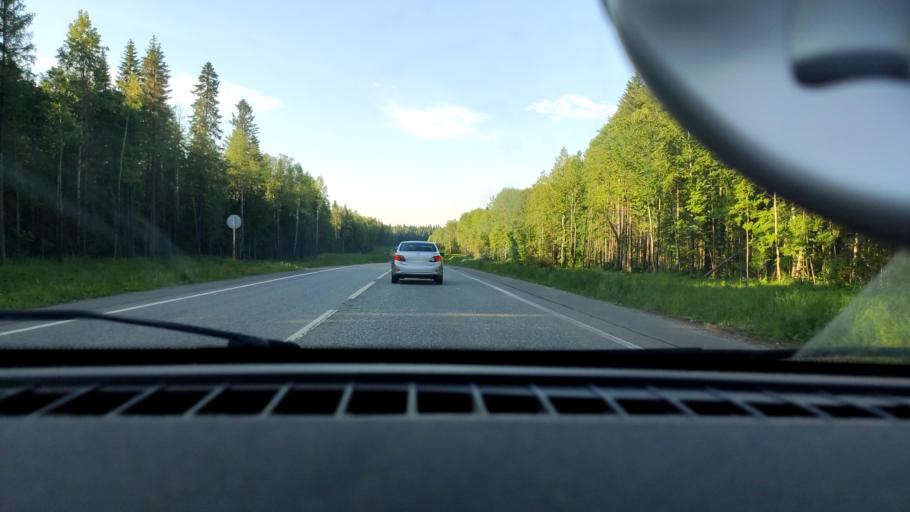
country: RU
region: Perm
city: Novyye Lyady
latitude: 58.0410
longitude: 56.5403
